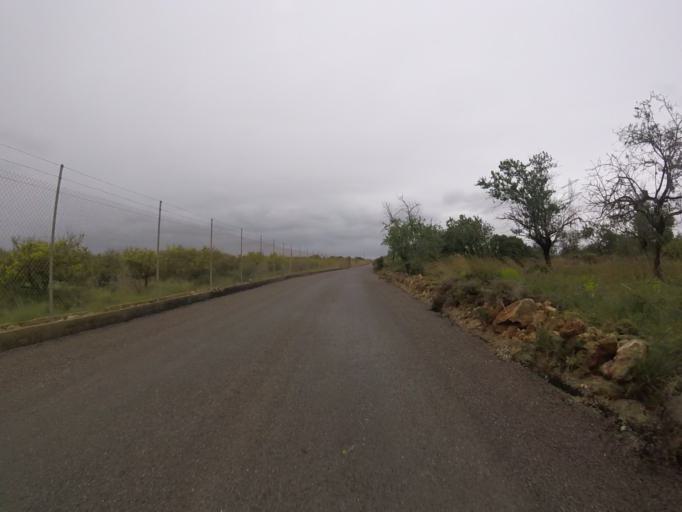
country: ES
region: Valencia
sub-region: Provincia de Castello
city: Alcoceber
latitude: 40.2373
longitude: 0.2523
